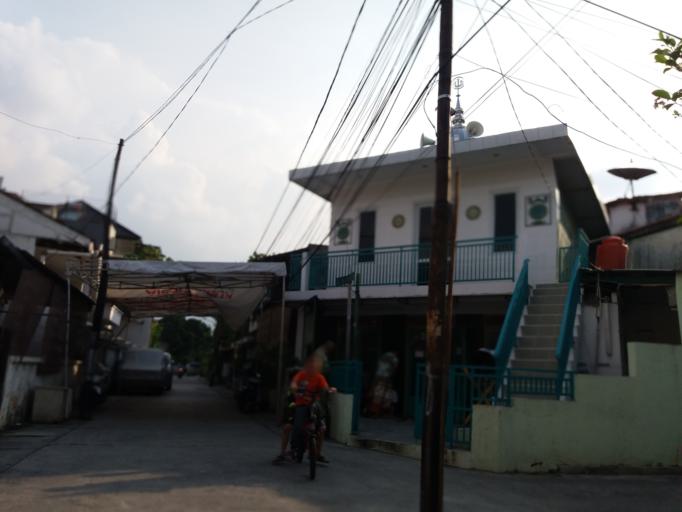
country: ID
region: Jakarta Raya
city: Jakarta
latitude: -6.2458
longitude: 106.8090
